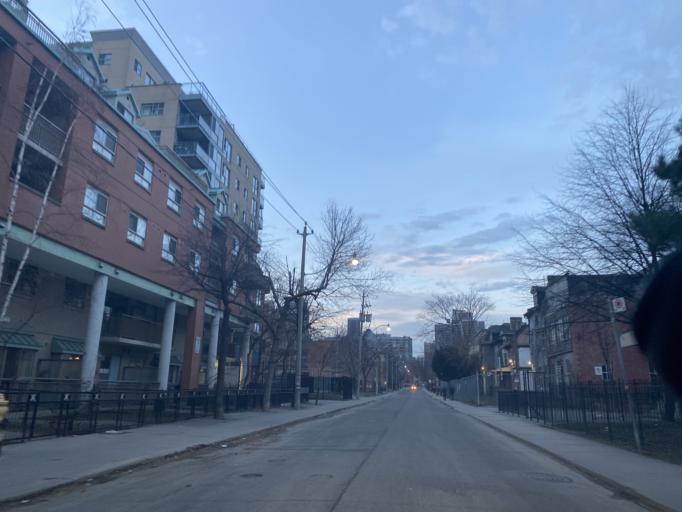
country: CA
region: Ontario
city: Toronto
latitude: 43.6582
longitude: -79.3738
